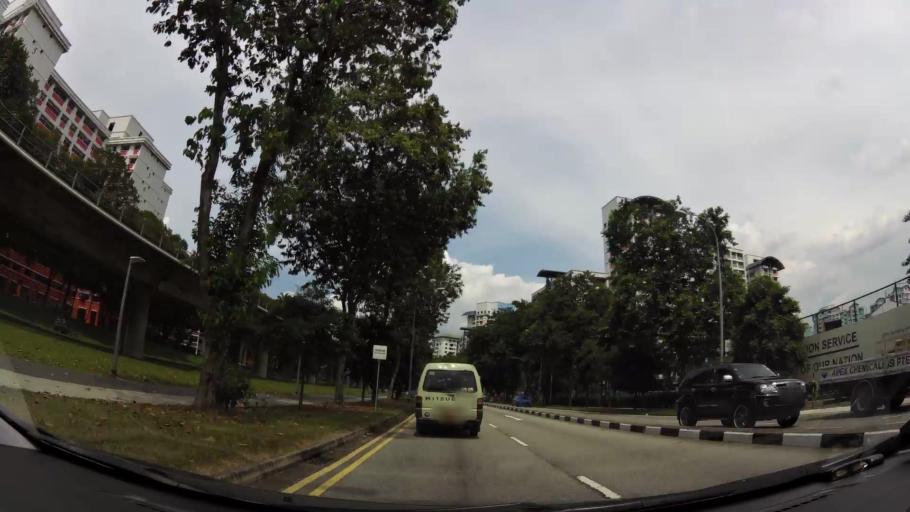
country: MY
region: Johor
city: Johor Bahru
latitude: 1.3943
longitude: 103.7463
